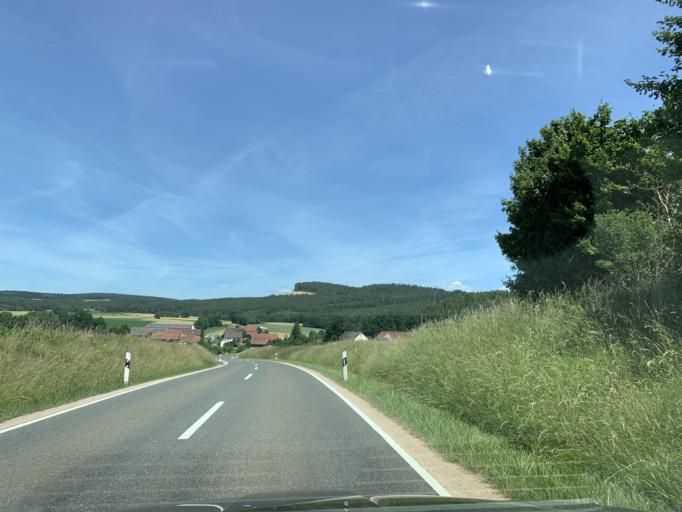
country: DE
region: Bavaria
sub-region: Upper Palatinate
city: Schwarzhofen
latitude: 49.3841
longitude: 12.3507
